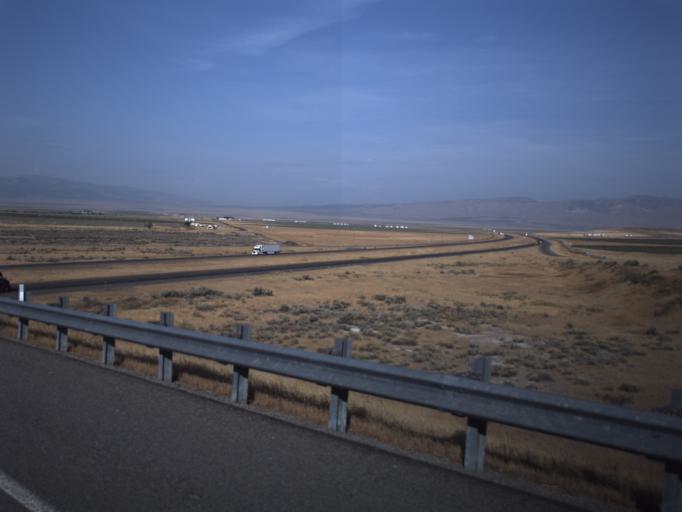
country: US
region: Idaho
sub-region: Oneida County
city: Malad City
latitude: 41.9653
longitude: -112.7555
